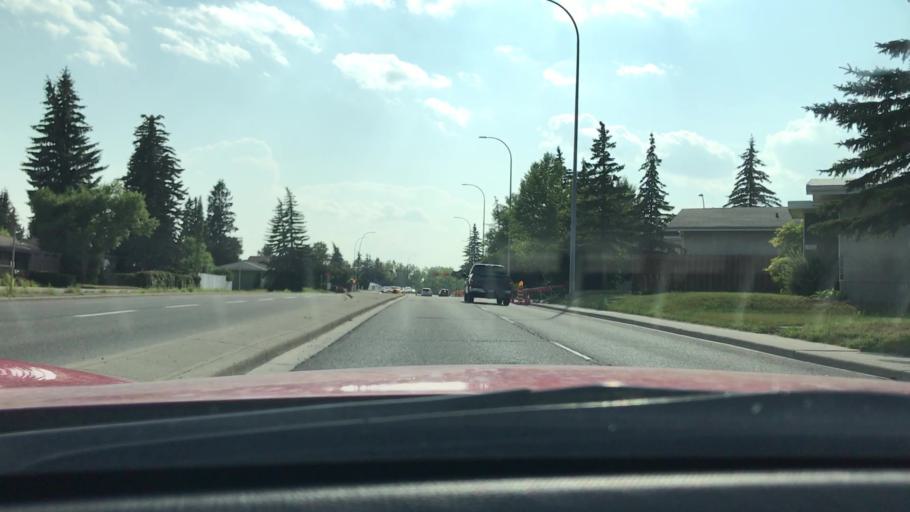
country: CA
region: Alberta
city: Calgary
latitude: 51.0197
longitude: -114.1502
